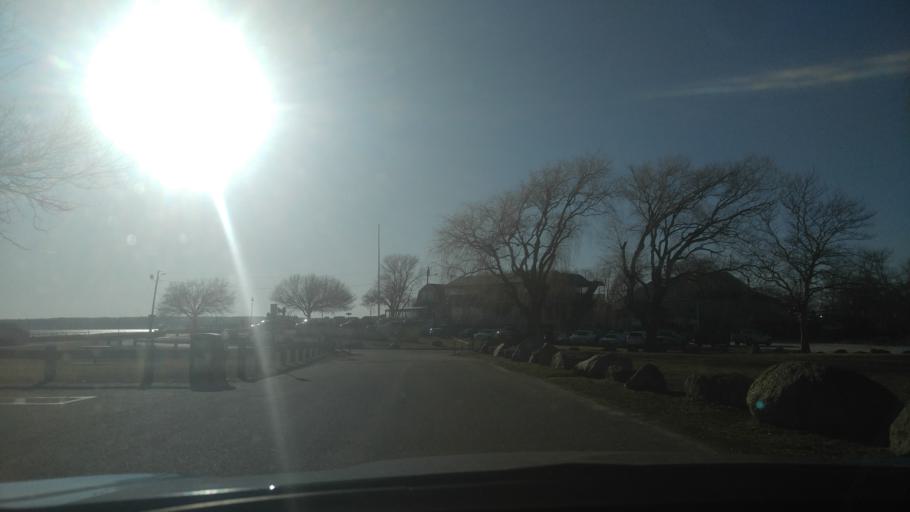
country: US
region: Rhode Island
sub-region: Kent County
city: Warwick
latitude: 41.6844
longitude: -71.3963
